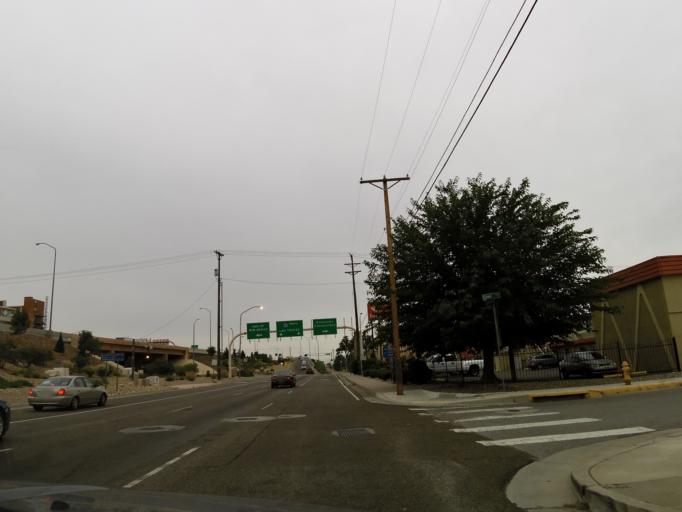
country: US
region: New Mexico
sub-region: Bernalillo County
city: Albuquerque
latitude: 35.0839
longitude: -106.6372
